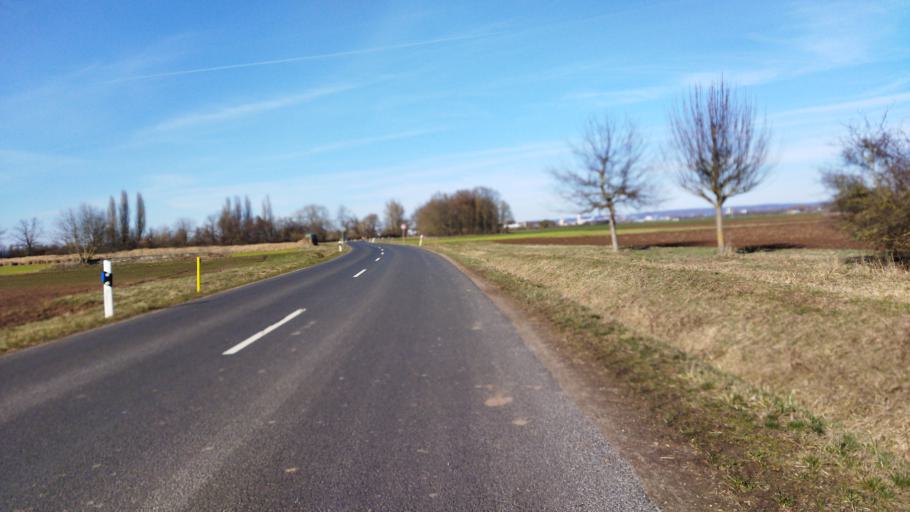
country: DE
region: Bavaria
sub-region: Regierungsbezirk Unterfranken
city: Grafenrheinfeld
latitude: 49.9862
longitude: 10.1993
